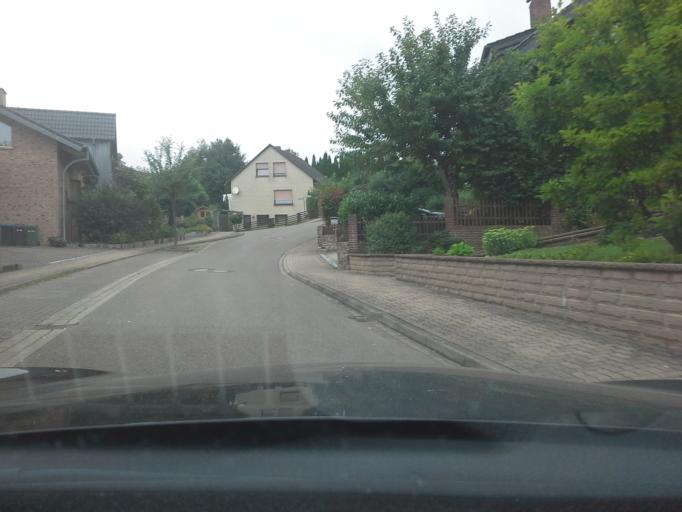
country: DE
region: Lower Saxony
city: Lauenau
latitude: 52.2781
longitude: 9.3742
